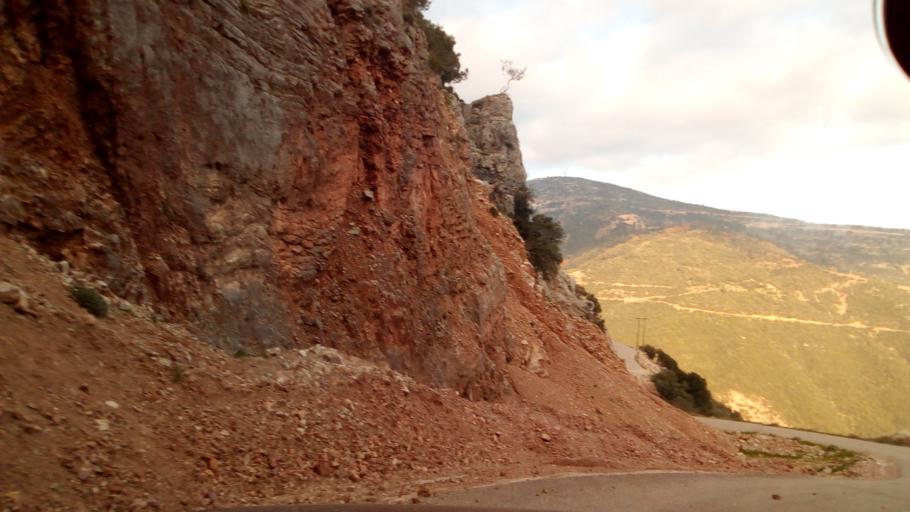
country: GR
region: West Greece
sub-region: Nomos Aitolias kai Akarnanias
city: Nafpaktos
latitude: 38.4276
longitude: 21.8196
